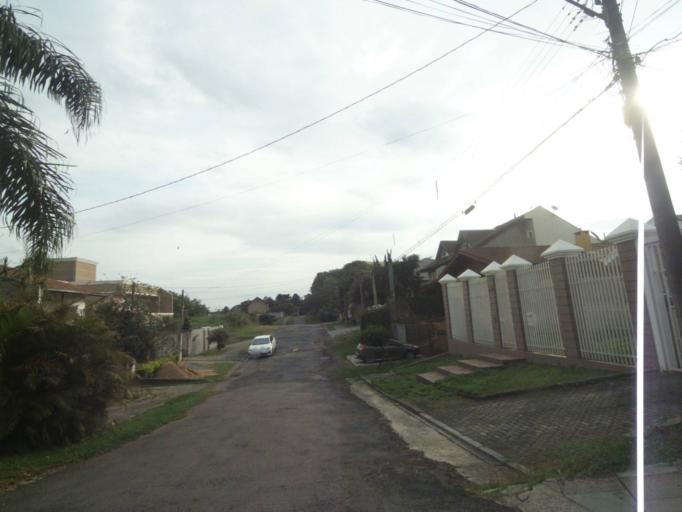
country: BR
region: Parana
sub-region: Curitiba
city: Curitiba
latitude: -25.3973
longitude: -49.2936
